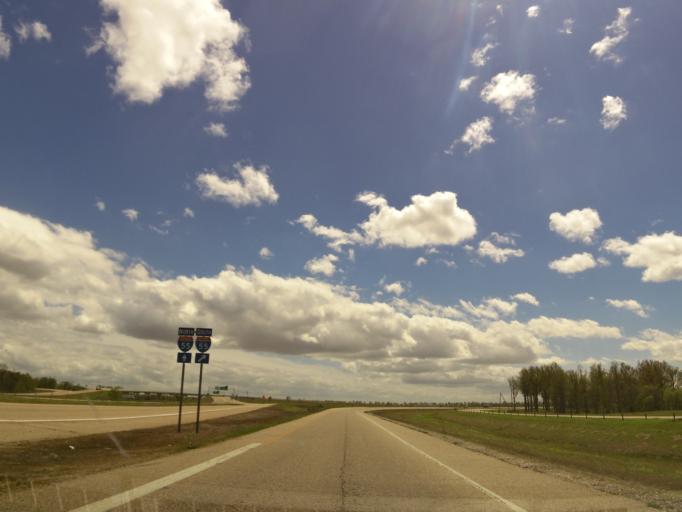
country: US
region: Arkansas
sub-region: Crittenden County
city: Marion
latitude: 35.3962
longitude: -90.2760
